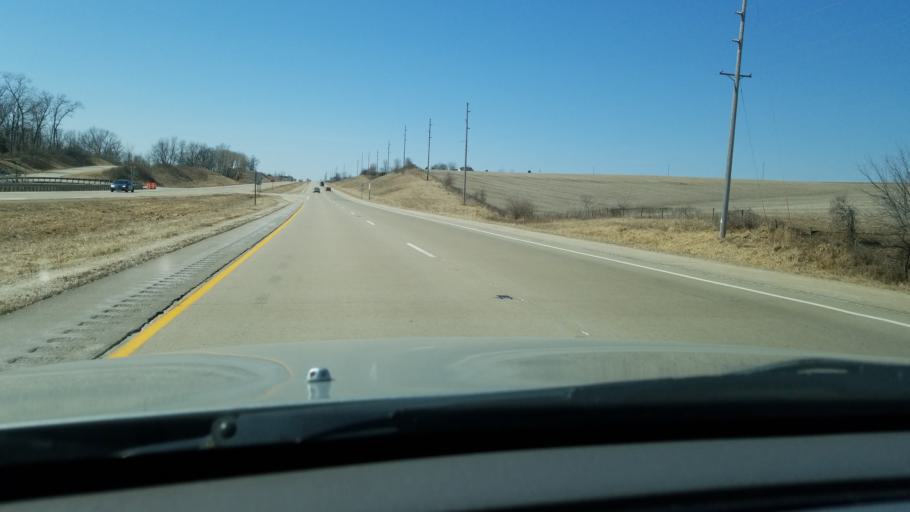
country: US
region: Wisconsin
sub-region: Dane County
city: Verona
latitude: 42.9886
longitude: -89.6175
